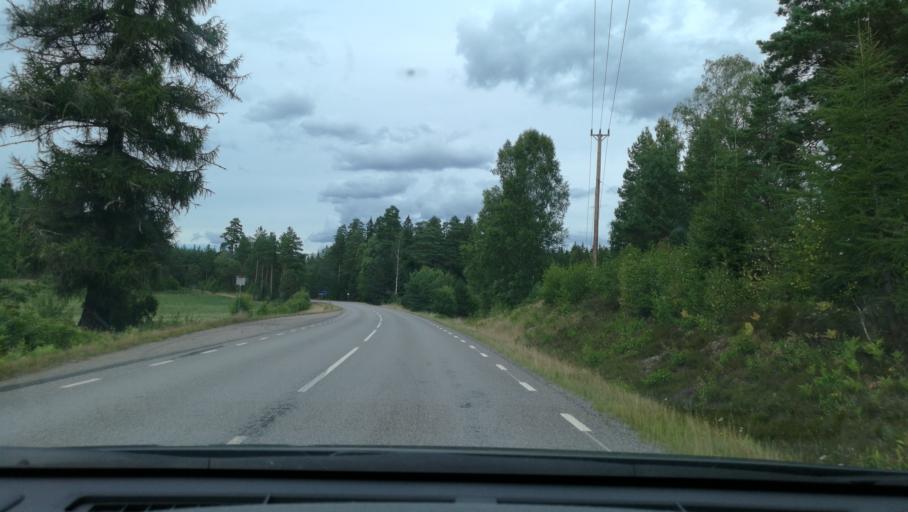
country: SE
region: OEstergoetland
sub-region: Norrkopings Kommun
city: Svartinge
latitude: 58.7525
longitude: 15.9793
